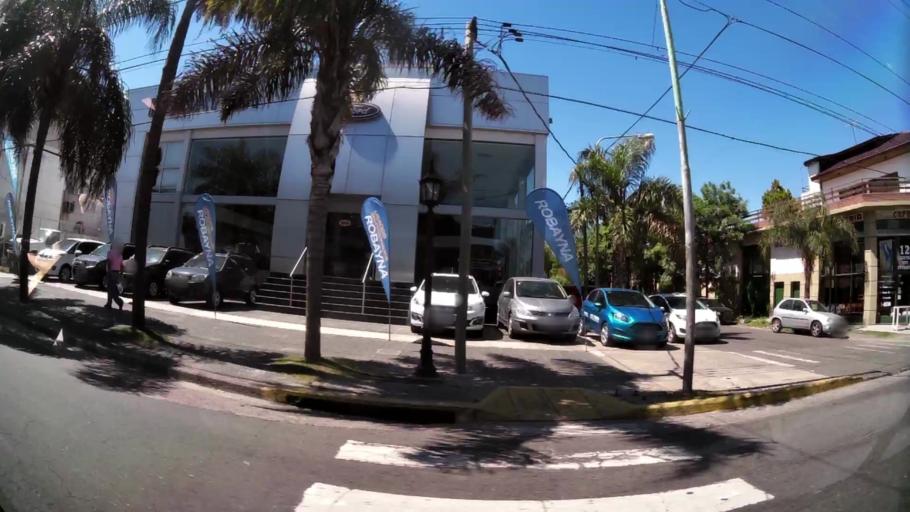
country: AR
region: Buenos Aires
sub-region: Partido de Tigre
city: Tigre
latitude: -34.4971
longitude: -58.6368
